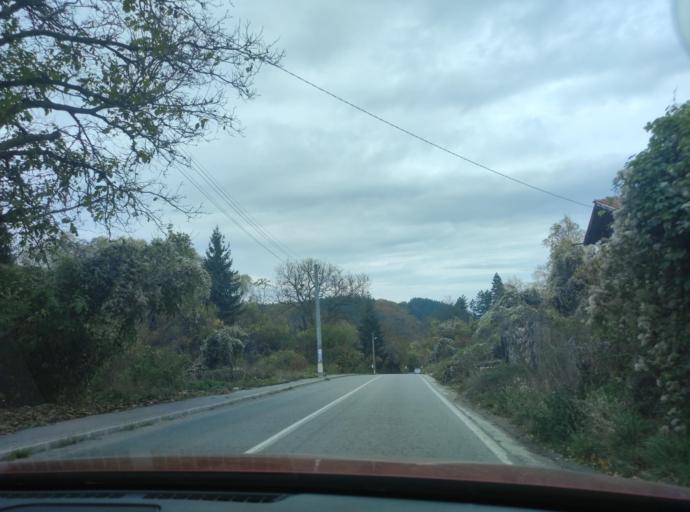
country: BG
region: Sofiya
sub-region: Obshtina Godech
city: Godech
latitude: 42.9715
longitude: 23.1415
